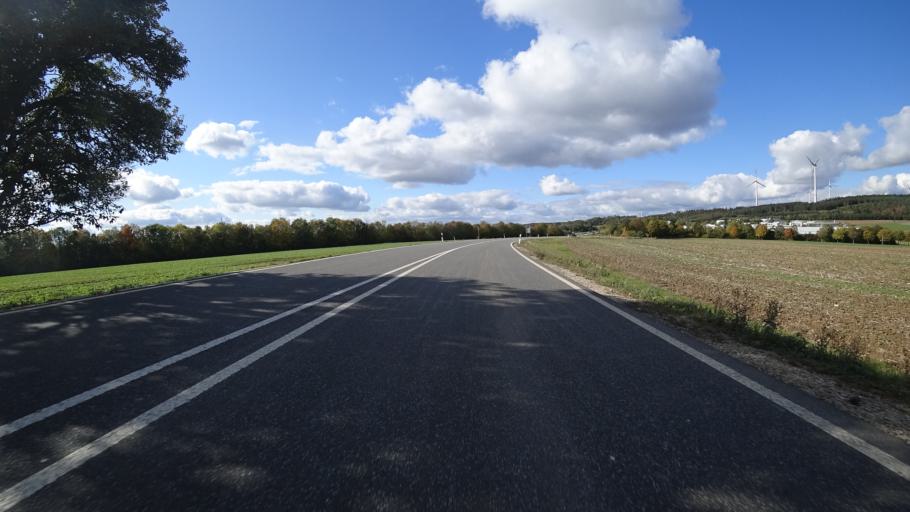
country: DE
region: Rheinland-Pfalz
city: Wiebelsheim
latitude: 50.0727
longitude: 7.6305
